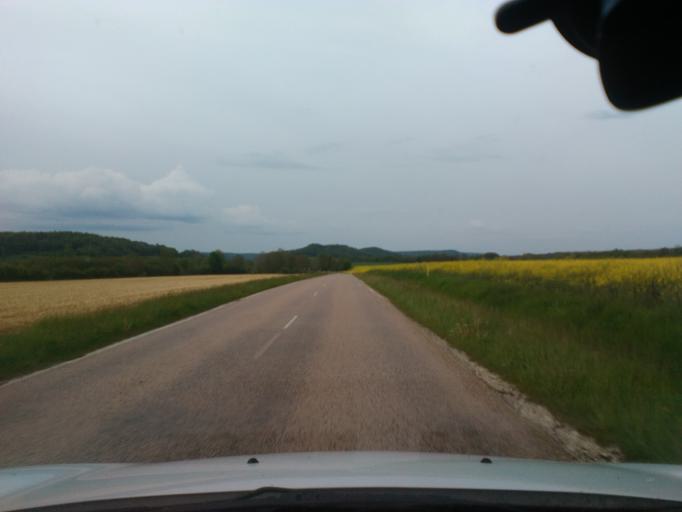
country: FR
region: Champagne-Ardenne
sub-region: Departement de la Haute-Marne
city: Doulaincourt-Saucourt
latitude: 48.2321
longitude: 5.2738
